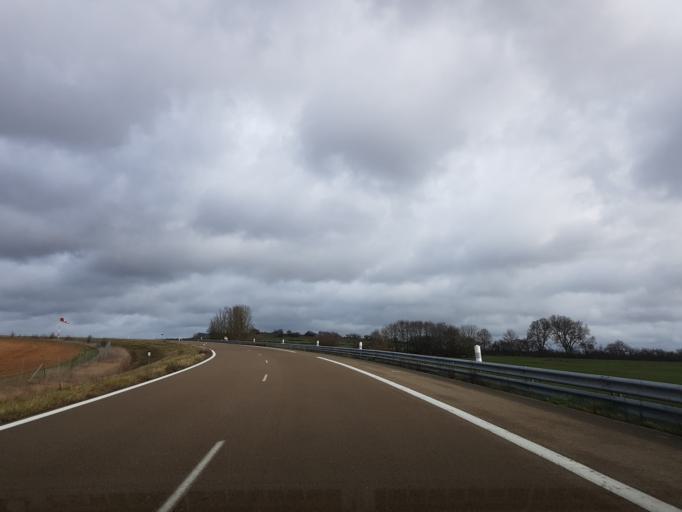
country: FR
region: Champagne-Ardenne
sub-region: Departement de la Haute-Marne
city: Rolampont
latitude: 47.9095
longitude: 5.2258
